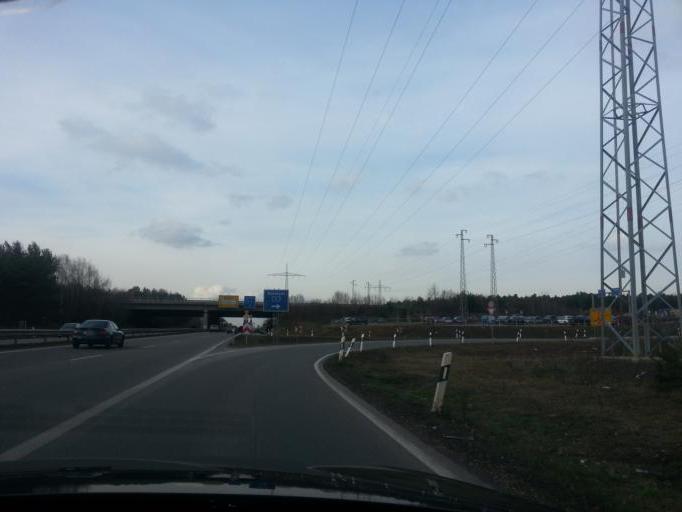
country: DE
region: Rheinland-Pfalz
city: Katzweiler
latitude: 49.4462
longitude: 7.7045
